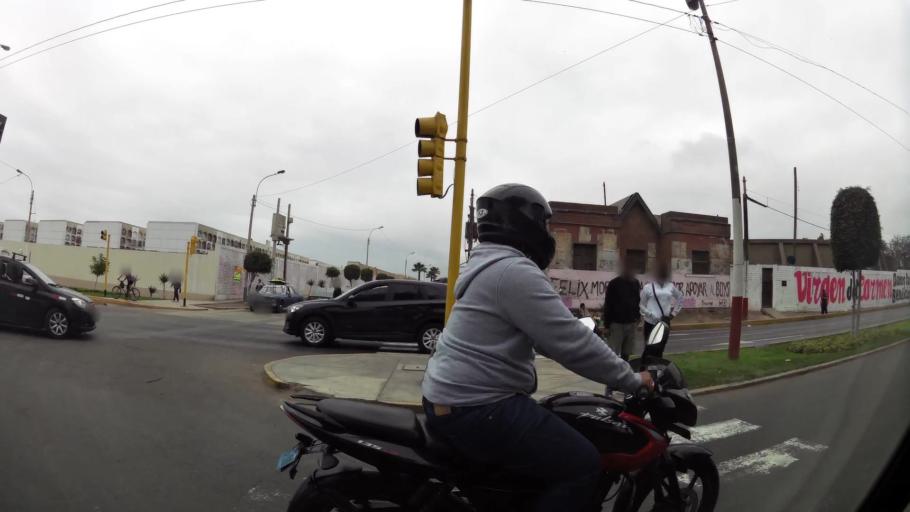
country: PE
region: Callao
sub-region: Callao
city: Callao
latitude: -12.0576
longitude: -77.1176
